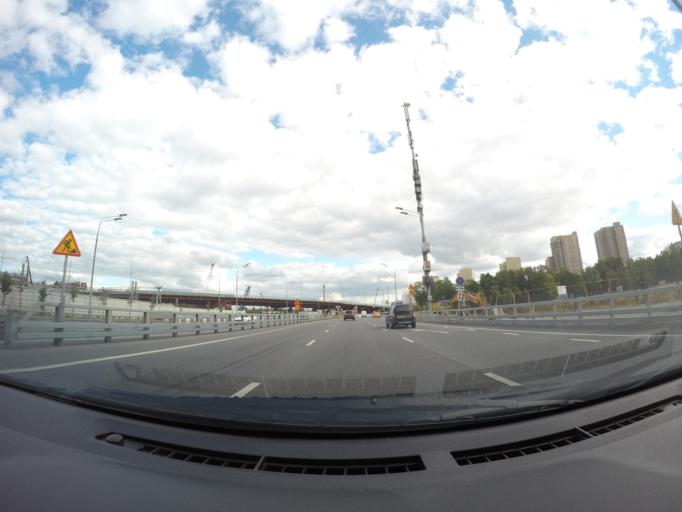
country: RU
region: Moscow
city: Likhobory
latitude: 55.8387
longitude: 37.5687
